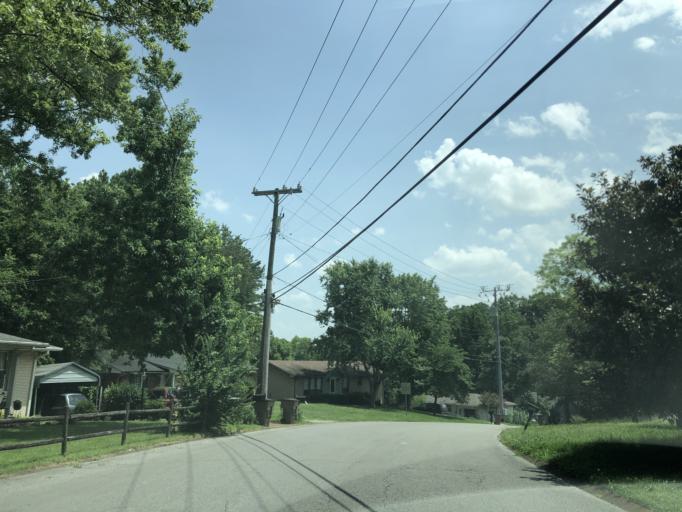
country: US
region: Tennessee
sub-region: Williamson County
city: Brentwood Estates
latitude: 36.0549
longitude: -86.6908
